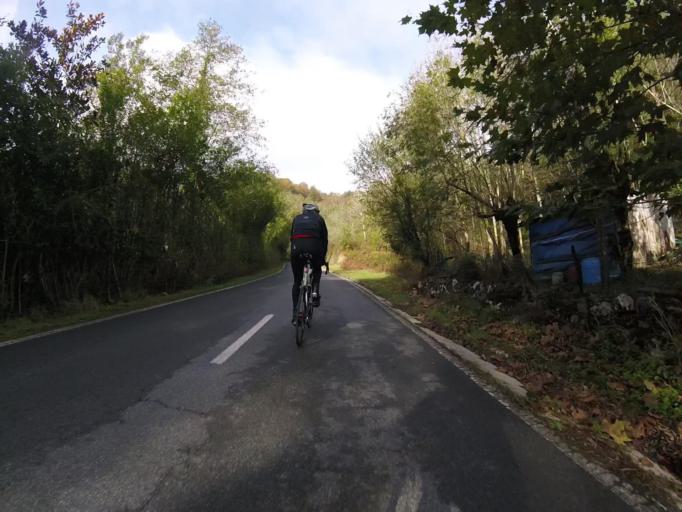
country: ES
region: Navarre
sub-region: Provincia de Navarra
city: Goizueta
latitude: 43.1916
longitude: -1.8583
